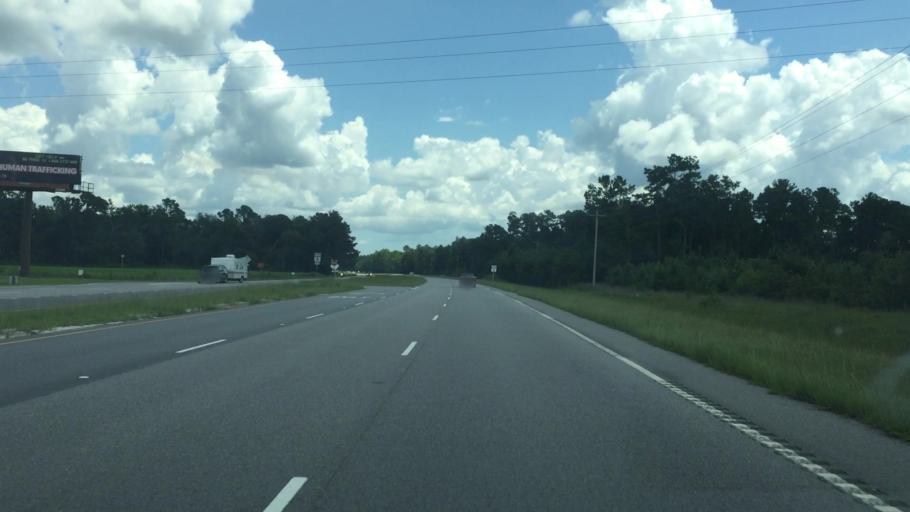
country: US
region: South Carolina
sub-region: Horry County
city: Loris
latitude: 34.0487
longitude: -78.8351
